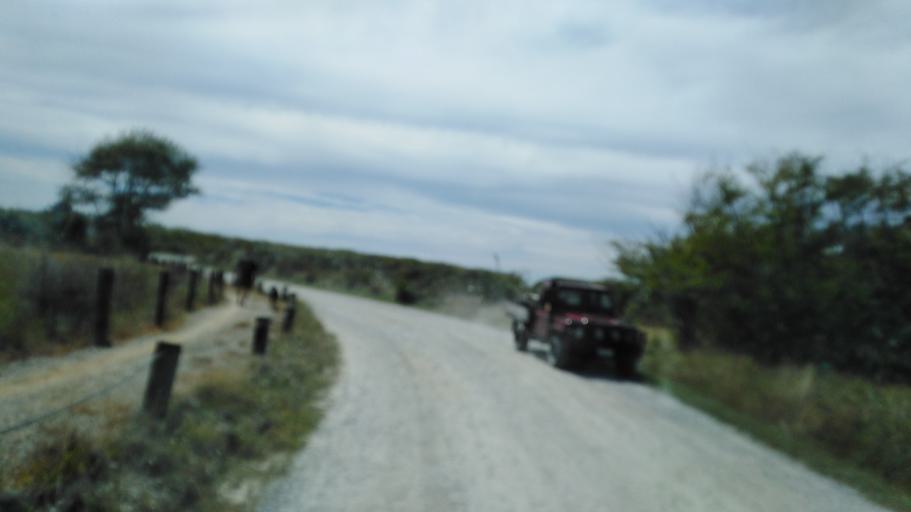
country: NZ
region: West Coast
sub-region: Buller District
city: Westport
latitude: -41.7377
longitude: 171.6045
